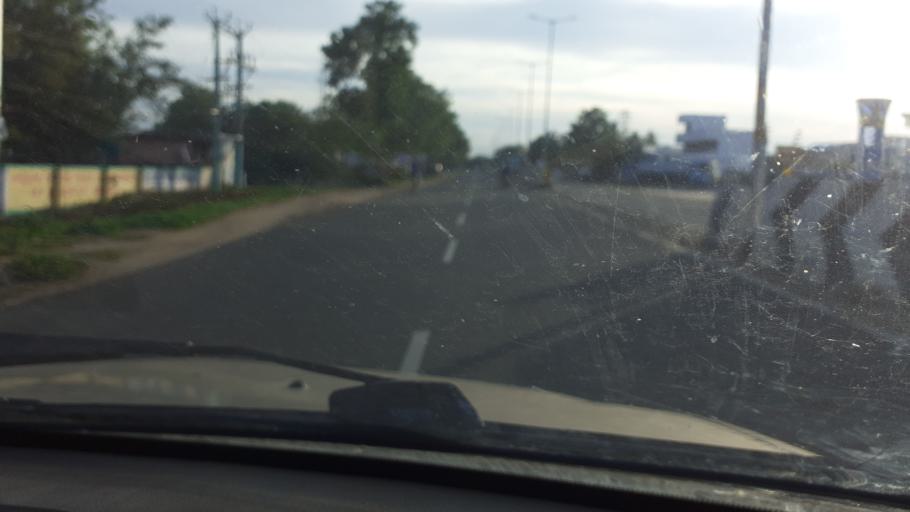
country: IN
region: Tamil Nadu
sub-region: Tirunelveli Kattabo
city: Tirunelveli
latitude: 8.6757
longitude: 77.7210
